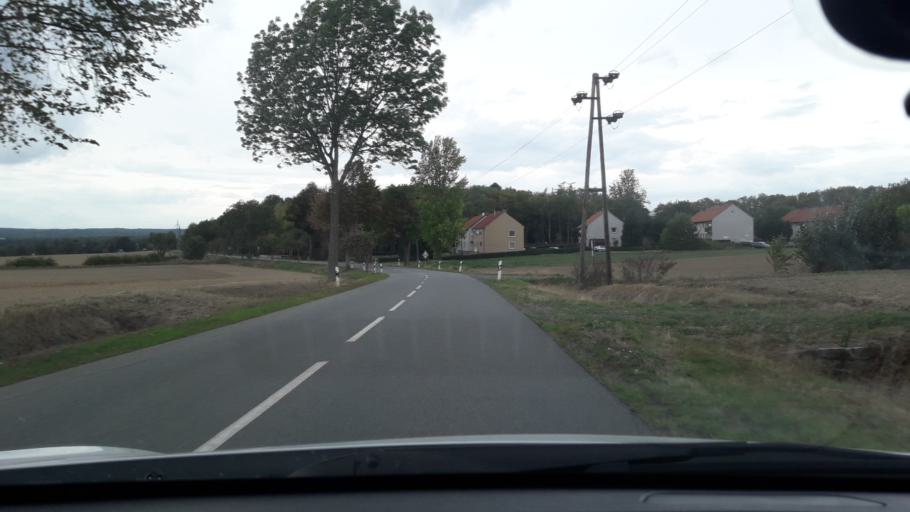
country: DE
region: Lower Saxony
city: Flothe
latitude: 52.0585
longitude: 10.4622
